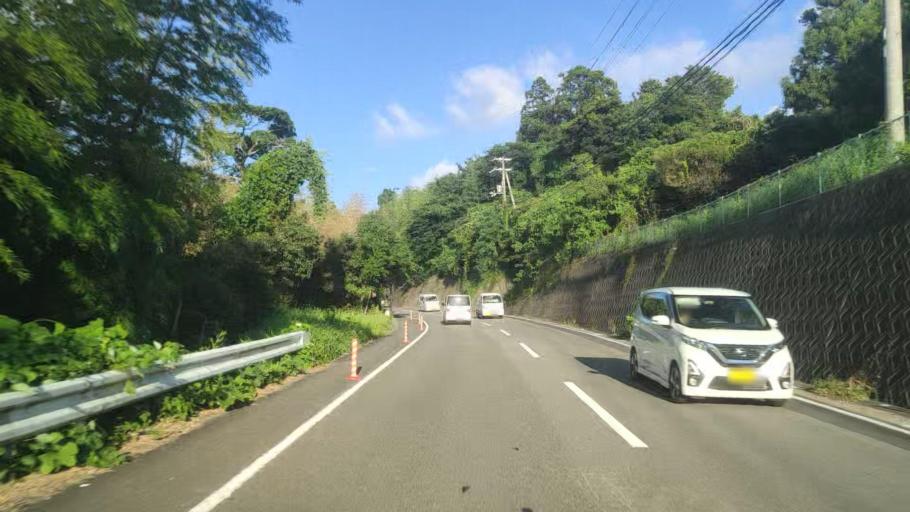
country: JP
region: Wakayama
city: Tanabe
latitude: 33.7344
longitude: 135.4299
